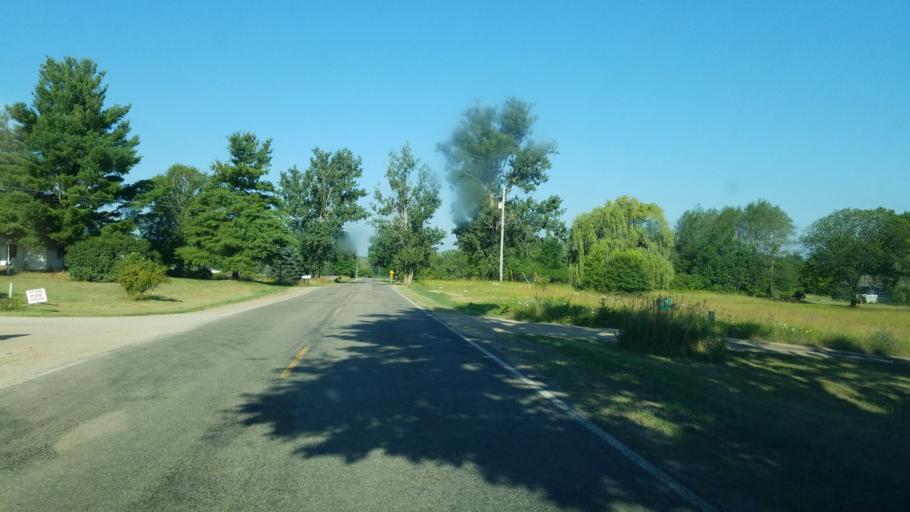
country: US
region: Michigan
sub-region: Montcalm County
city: Howard City
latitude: 43.4903
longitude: -85.4259
